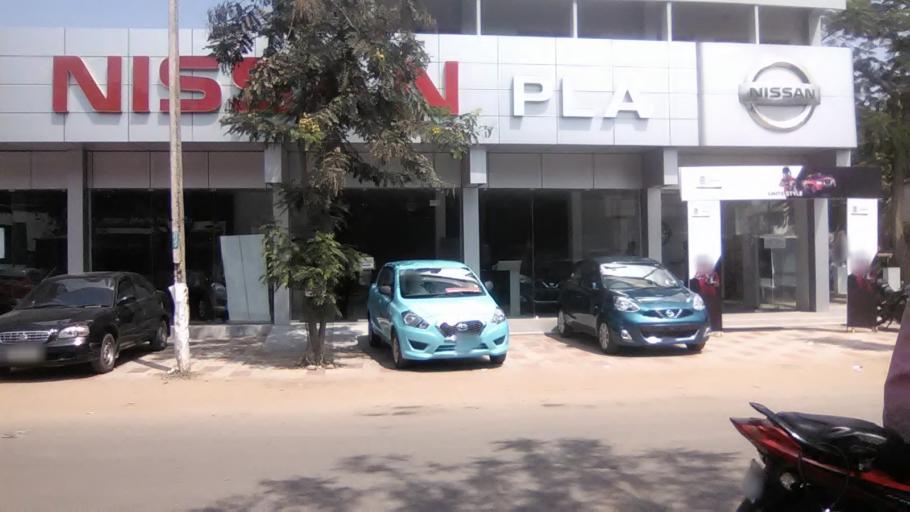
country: IN
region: Tamil Nadu
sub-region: Tiruchchirappalli
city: Tiruchirappalli
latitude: 10.8027
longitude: 78.6830
